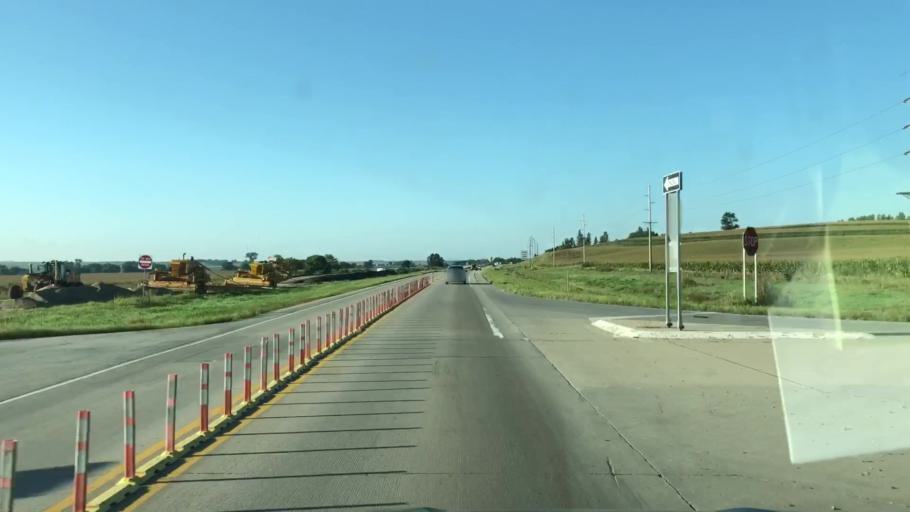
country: US
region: Iowa
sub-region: Plymouth County
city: Le Mars
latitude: 42.7462
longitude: -96.2132
